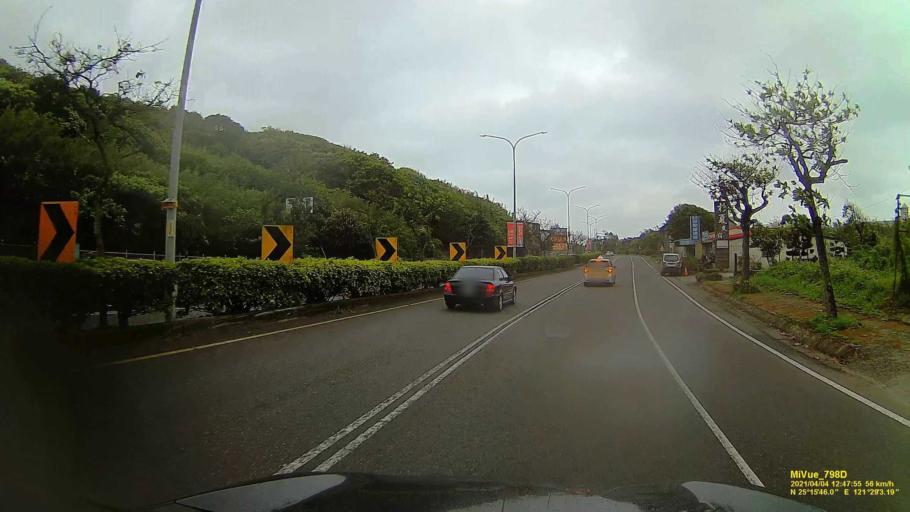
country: TW
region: Taipei
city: Taipei
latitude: 25.2629
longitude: 121.4840
